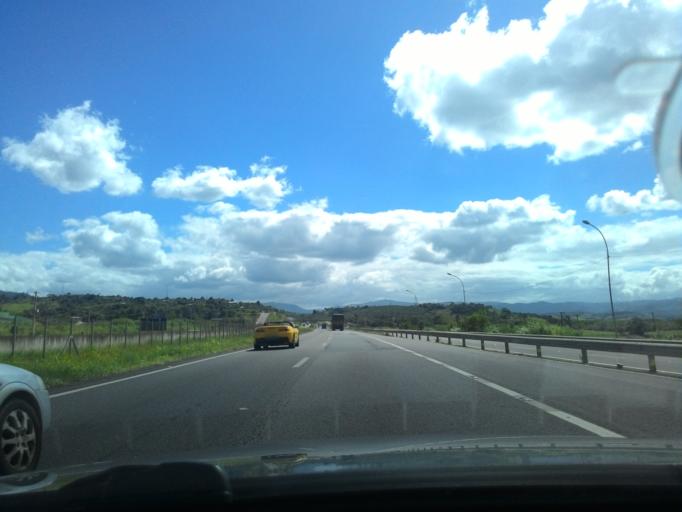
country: BR
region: Sao Paulo
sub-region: Cajati
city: Cajati
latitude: -24.7328
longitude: -48.1129
